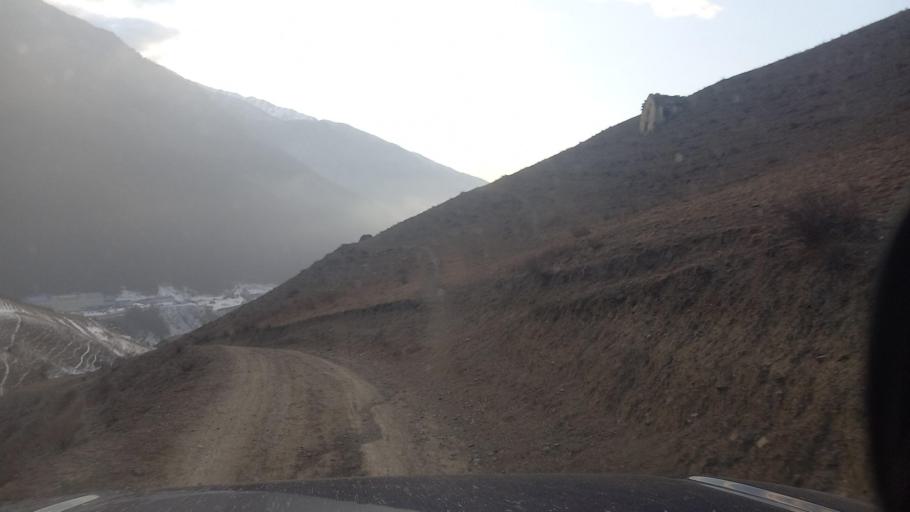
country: RU
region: Ingushetiya
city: Dzhayrakh
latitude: 42.8053
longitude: 44.7607
